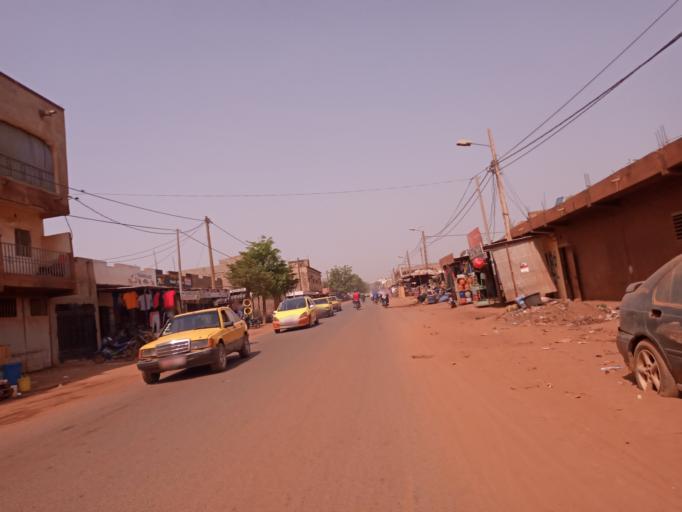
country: ML
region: Bamako
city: Bamako
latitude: 12.5888
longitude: -7.9827
